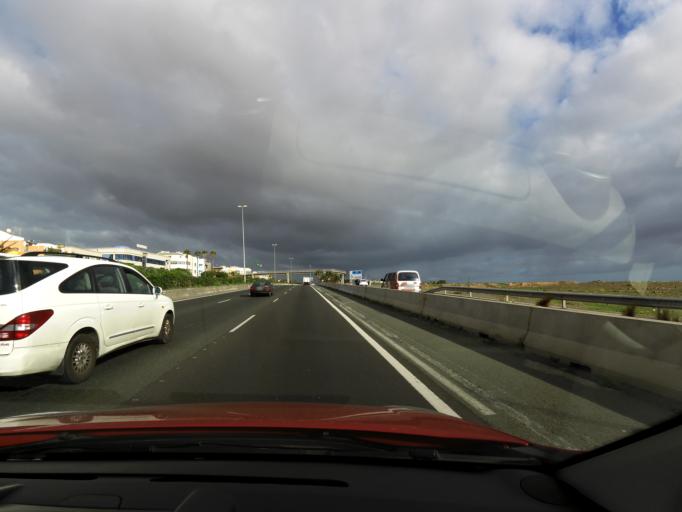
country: ES
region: Canary Islands
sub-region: Provincia de Las Palmas
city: Telde
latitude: 27.9836
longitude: -15.3920
